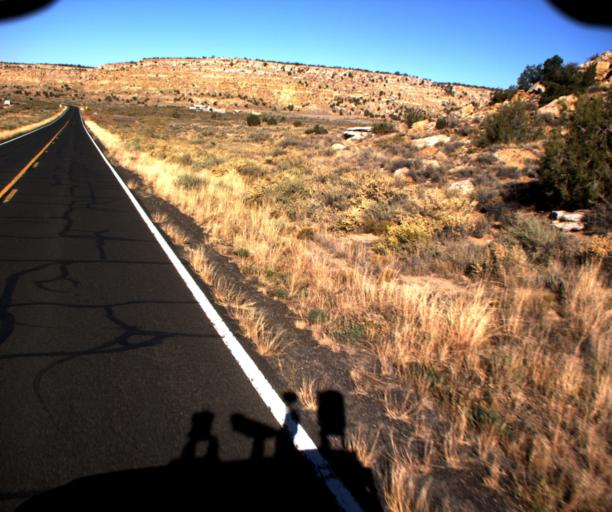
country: US
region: Arizona
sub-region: Navajo County
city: First Mesa
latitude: 35.8403
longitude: -110.2373
